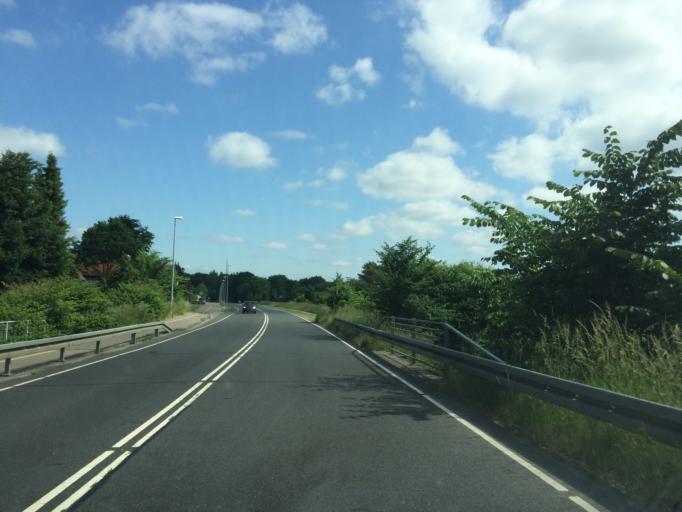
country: DK
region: Central Jutland
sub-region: Silkeborg Kommune
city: Silkeborg
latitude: 56.1570
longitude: 9.5139
